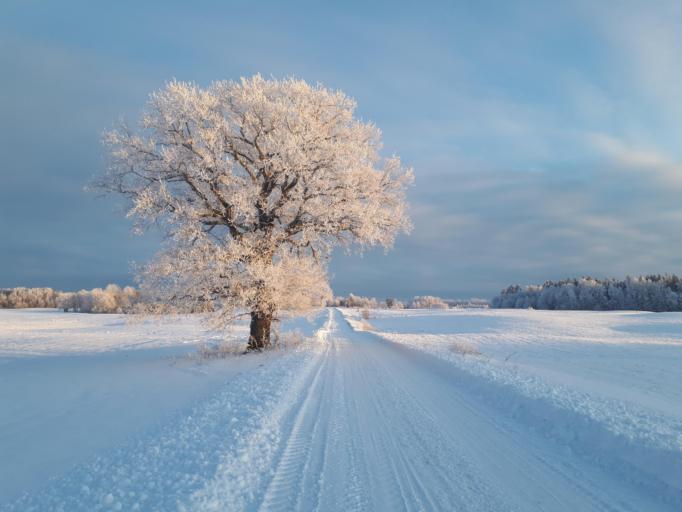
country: LT
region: Alytaus apskritis
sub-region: Alytaus rajonas
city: Daugai
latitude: 54.4439
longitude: 24.2291
